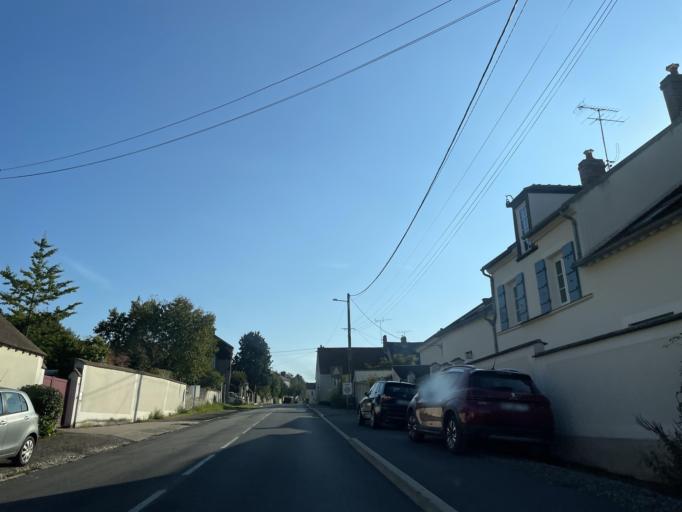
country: FR
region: Ile-de-France
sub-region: Departement de Seine-et-Marne
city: Voulangis
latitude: 48.8518
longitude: 2.8986
